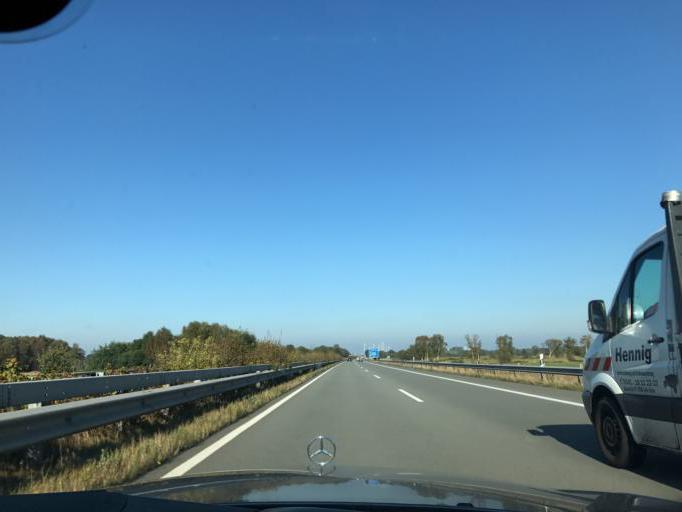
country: DE
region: Lower Saxony
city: Bunde
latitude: 53.1509
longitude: 7.2784
